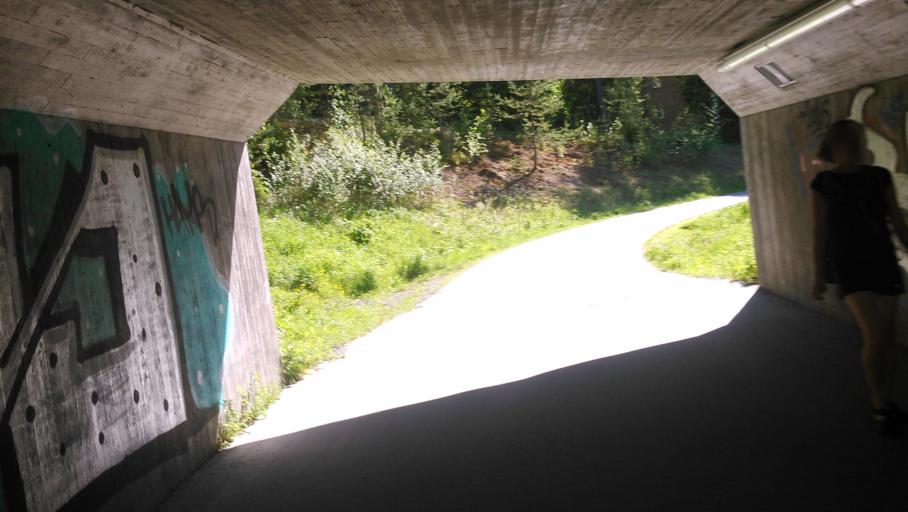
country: SE
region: Vaesterbotten
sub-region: Umea Kommun
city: Ersmark
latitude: 63.8282
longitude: 20.3154
